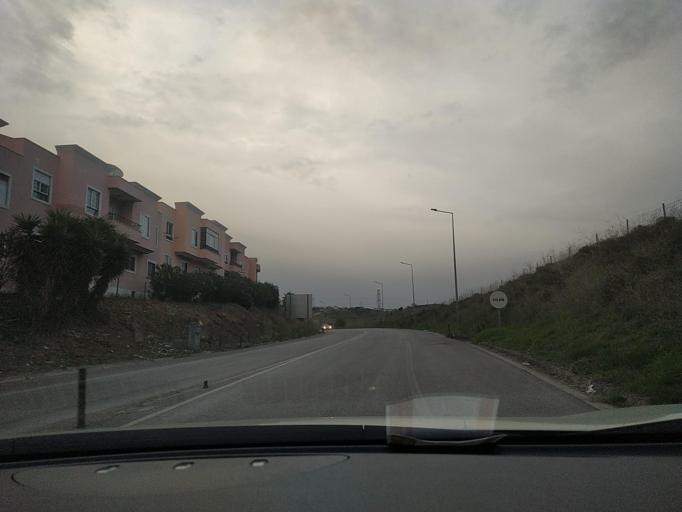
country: PT
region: Lisbon
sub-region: Loures
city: Santa Iria da Azoia
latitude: 38.8630
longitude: -9.1026
